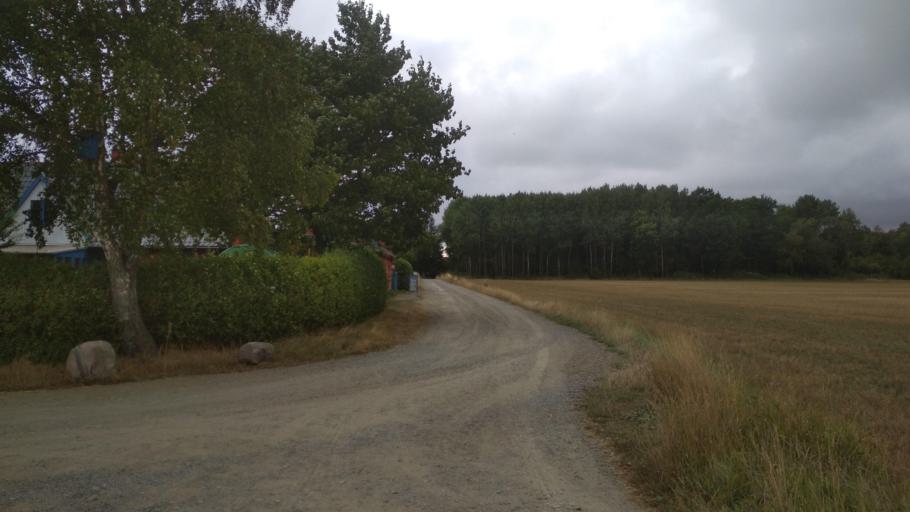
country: DK
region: Capital Region
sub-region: Bornholm Kommune
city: Akirkeby
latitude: 55.0608
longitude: 14.9541
